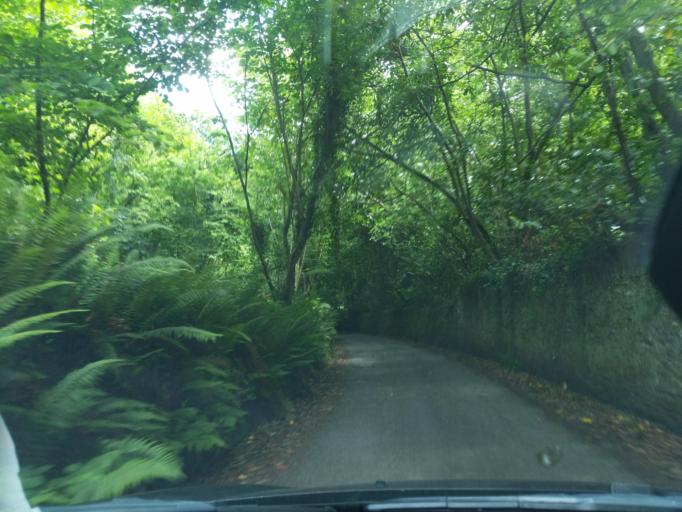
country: GB
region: England
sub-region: Devon
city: Plympton
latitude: 50.4078
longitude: -4.0891
